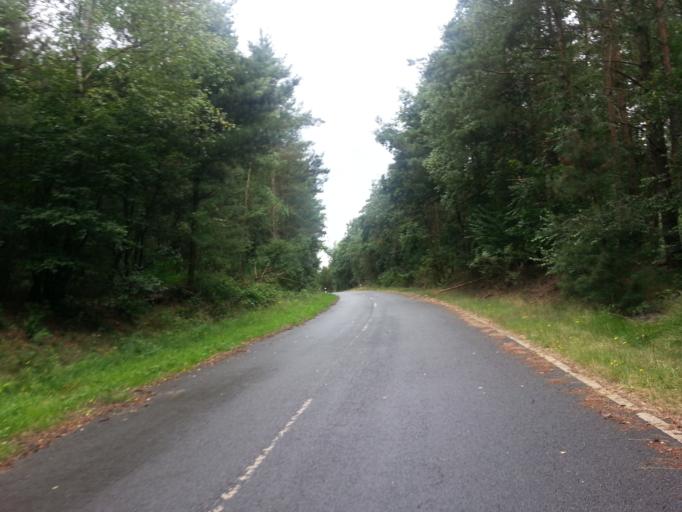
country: DE
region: North Rhine-Westphalia
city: Oer-Erkenschwick
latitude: 51.6967
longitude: 7.2616
